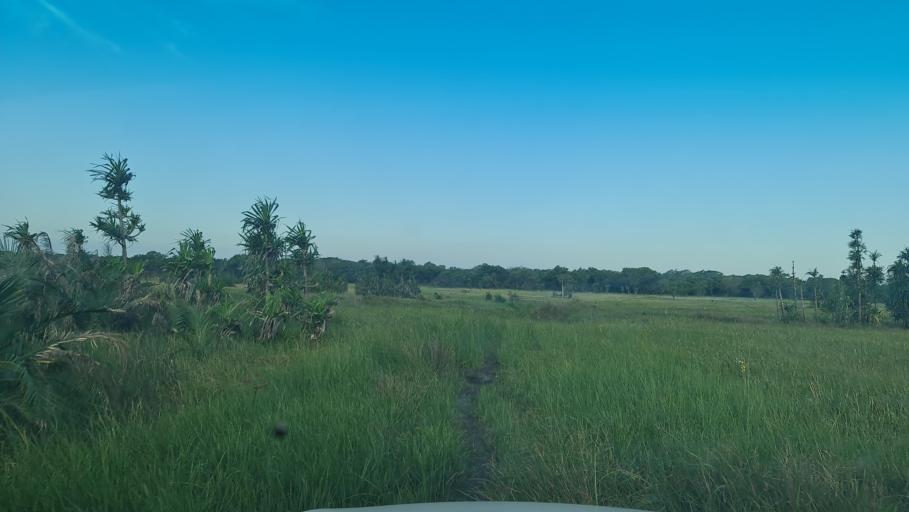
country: MZ
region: Gaza
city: Macia
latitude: -25.2126
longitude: 33.0566
